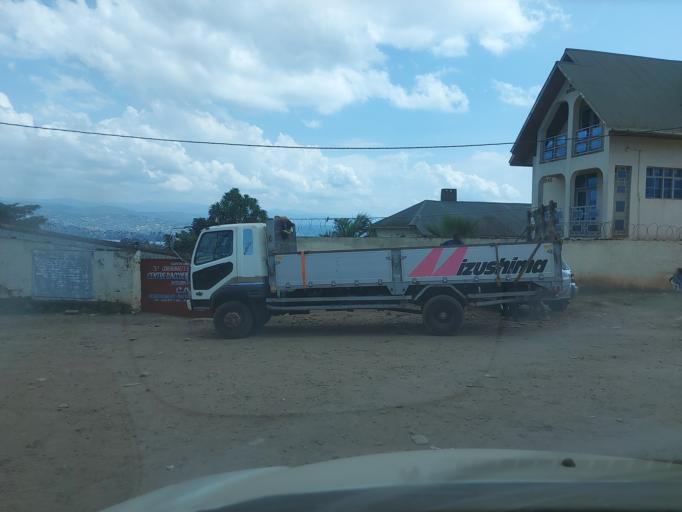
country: RW
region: Western Province
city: Cyangugu
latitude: -2.4955
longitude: 28.8884
